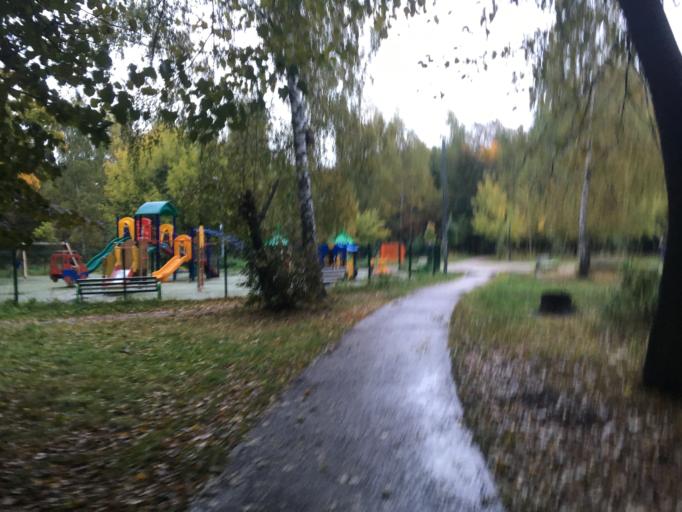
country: RU
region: Moskovskaya
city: Lyubertsy
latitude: 55.6945
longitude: 37.8814
